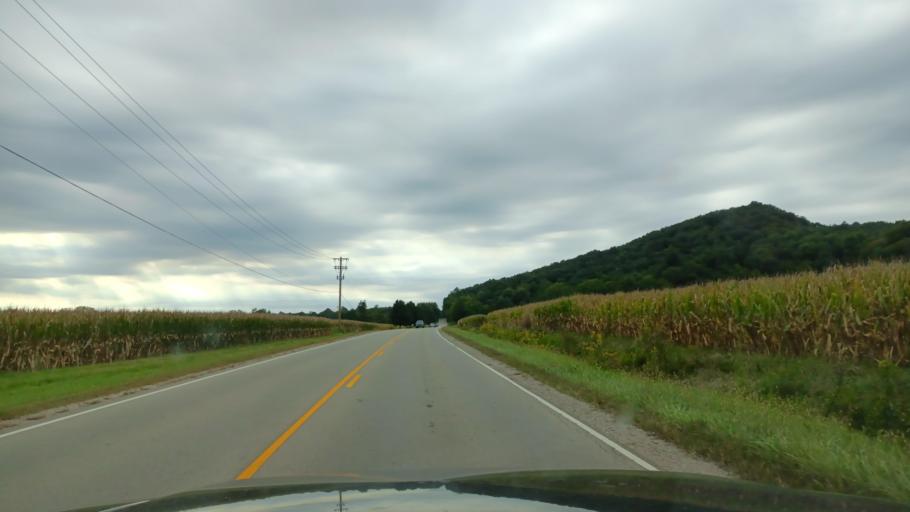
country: US
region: Ohio
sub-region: Ross County
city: Chillicothe
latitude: 39.2824
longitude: -82.8483
